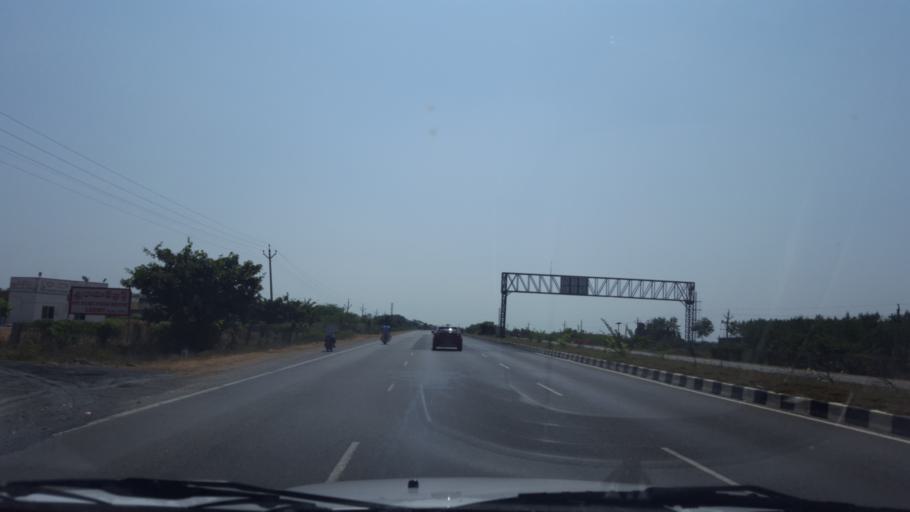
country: IN
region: Andhra Pradesh
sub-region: Prakasam
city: Addanki
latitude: 15.7164
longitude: 80.0142
